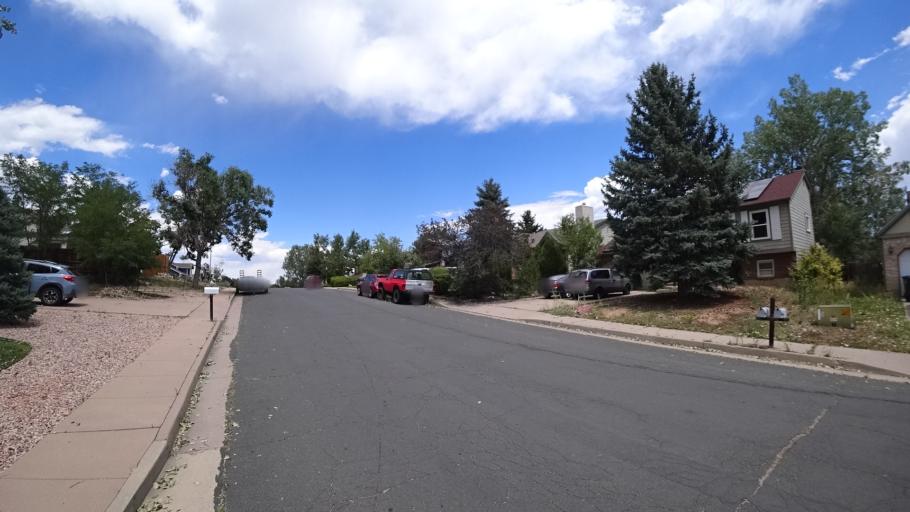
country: US
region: Colorado
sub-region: El Paso County
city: Stratmoor
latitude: 38.7844
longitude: -104.7992
